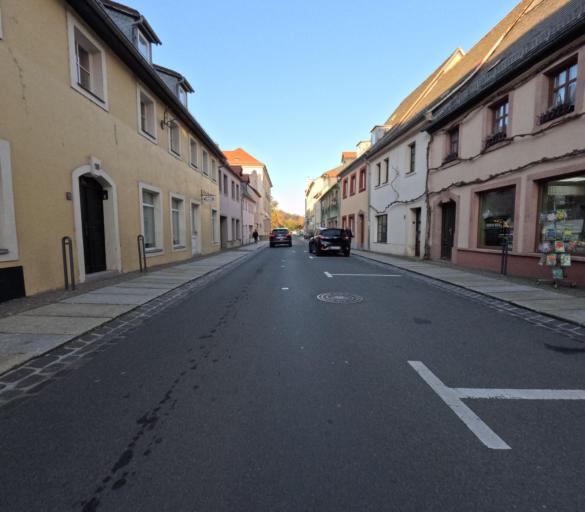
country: DE
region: Saxony
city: Grimma
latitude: 51.2379
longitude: 12.7306
